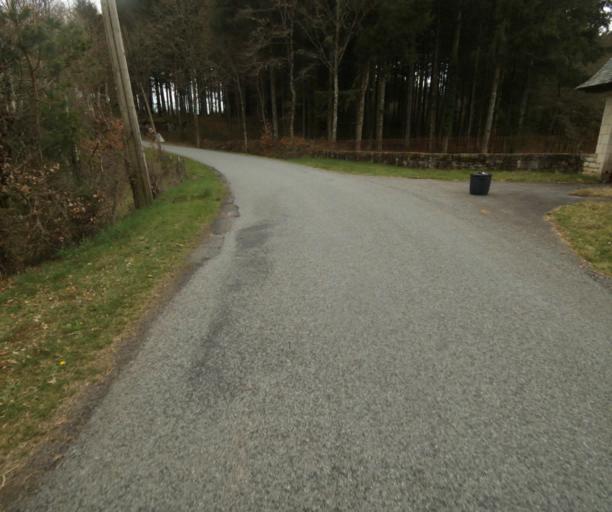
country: FR
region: Limousin
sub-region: Departement de la Correze
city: Correze
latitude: 45.3246
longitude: 1.9165
